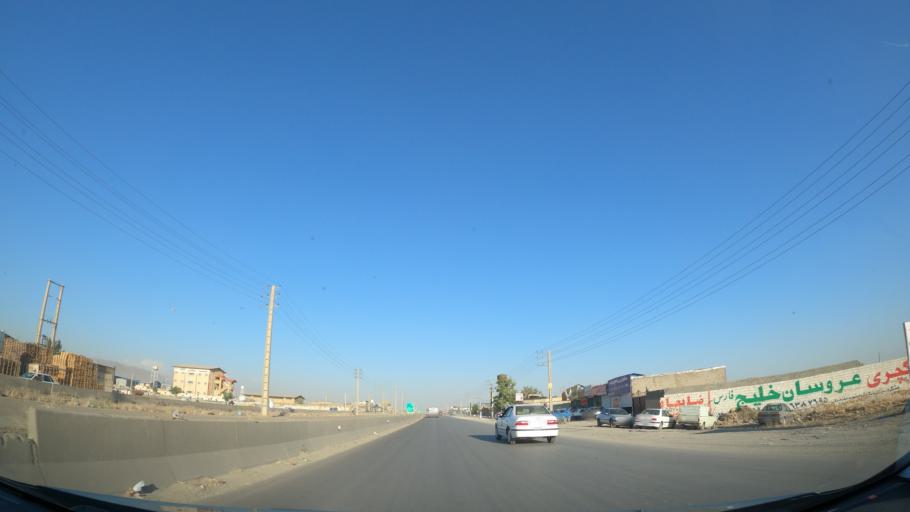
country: IR
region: Alborz
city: Hashtgerd
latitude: 35.9161
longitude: 50.7563
